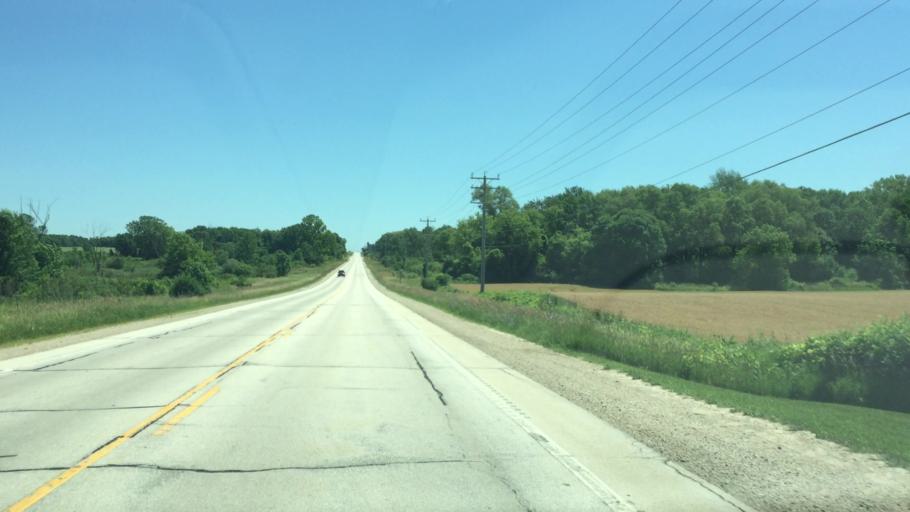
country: US
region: Wisconsin
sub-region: Calumet County
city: Sherwood
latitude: 44.1409
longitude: -88.2572
